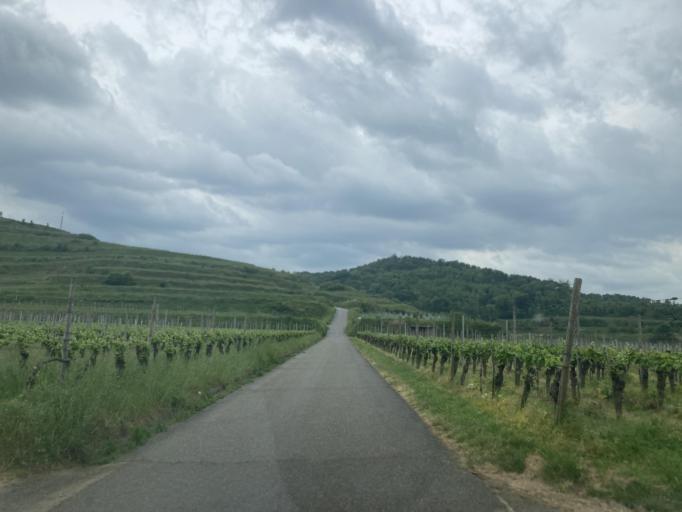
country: DE
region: Baden-Wuerttemberg
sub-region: Freiburg Region
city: Vogtsburg
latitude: 48.0923
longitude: 7.6502
